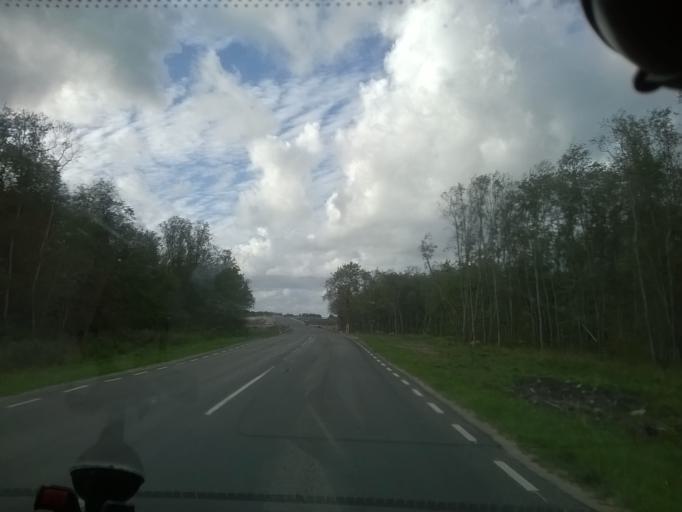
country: EE
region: Harju
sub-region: Rae vald
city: Jueri
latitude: 59.3700
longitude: 24.9161
